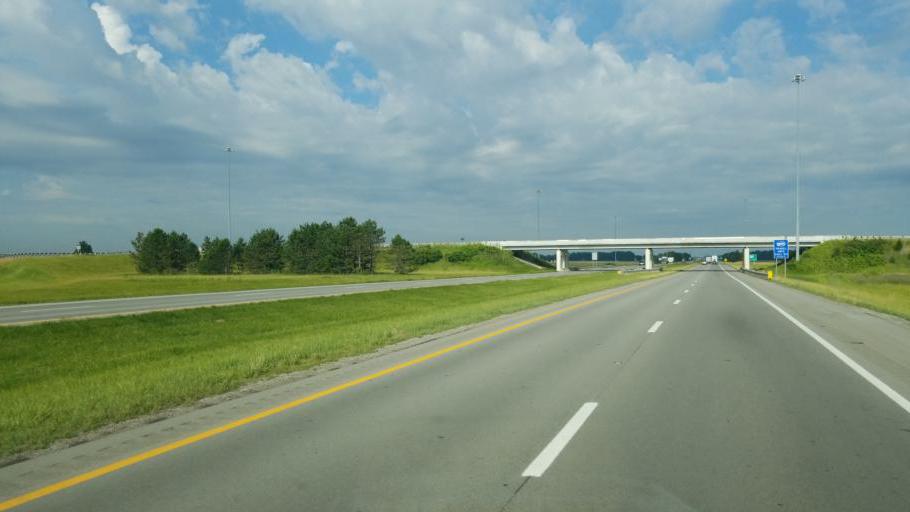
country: US
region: Ohio
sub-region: Wyandot County
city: Upper Sandusky
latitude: 40.8583
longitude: -83.2772
